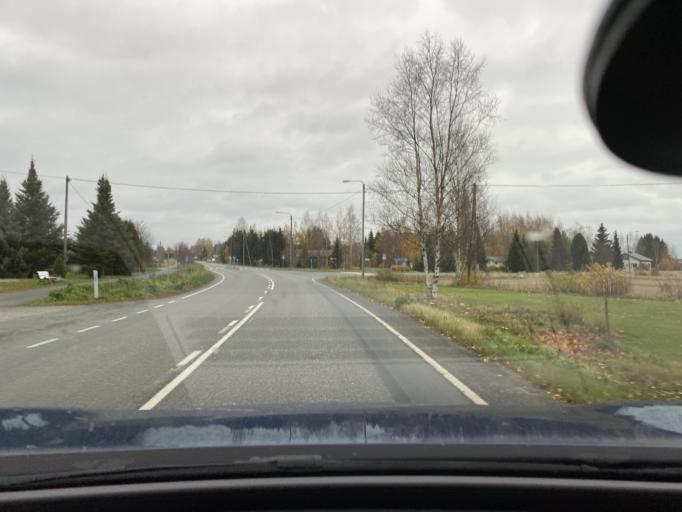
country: FI
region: Satakunta
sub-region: Pori
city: Vampula
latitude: 61.0664
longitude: 22.5208
